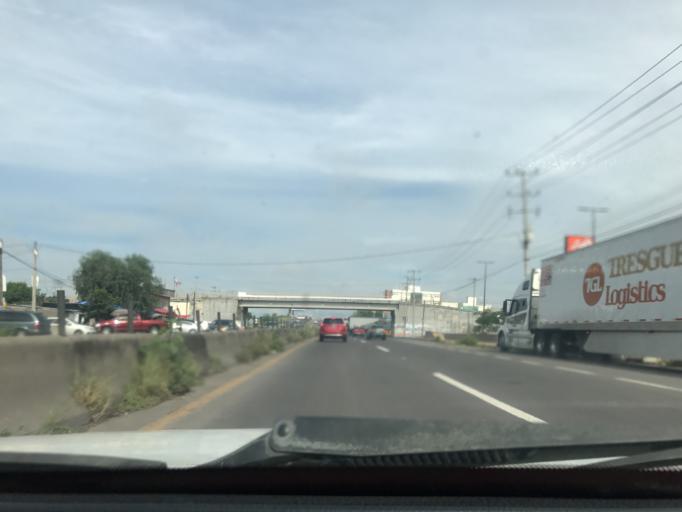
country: MX
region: Morelos
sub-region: Cuautla
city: Tierra Larga (Campo Nuevo)
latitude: 18.8492
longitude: -98.9344
